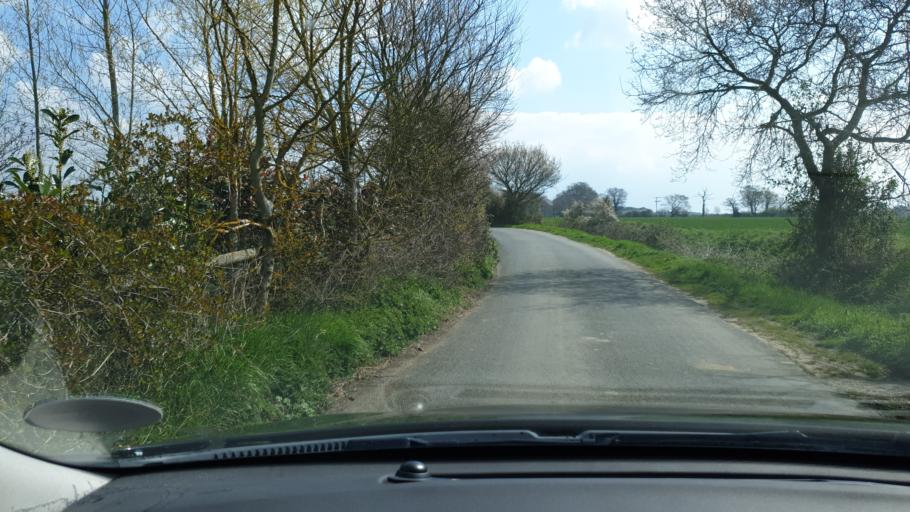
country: GB
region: England
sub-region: Essex
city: Great Bentley
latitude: 51.8414
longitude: 1.0773
